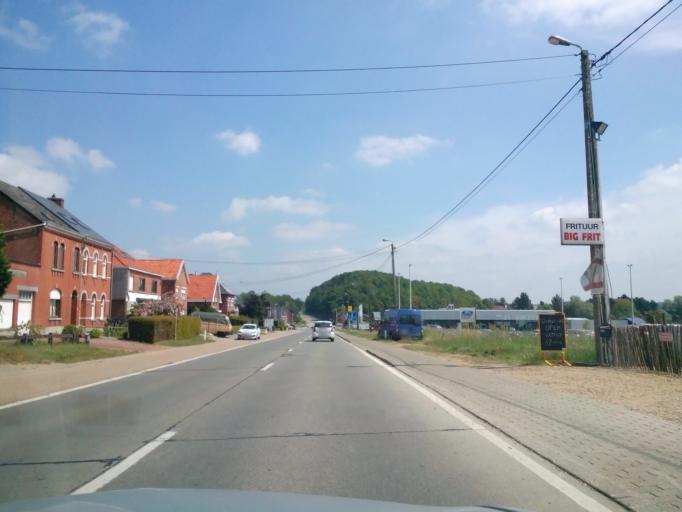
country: BE
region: Flanders
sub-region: Provincie Vlaams-Brabant
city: Holsbeek
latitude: 50.9647
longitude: 4.7859
